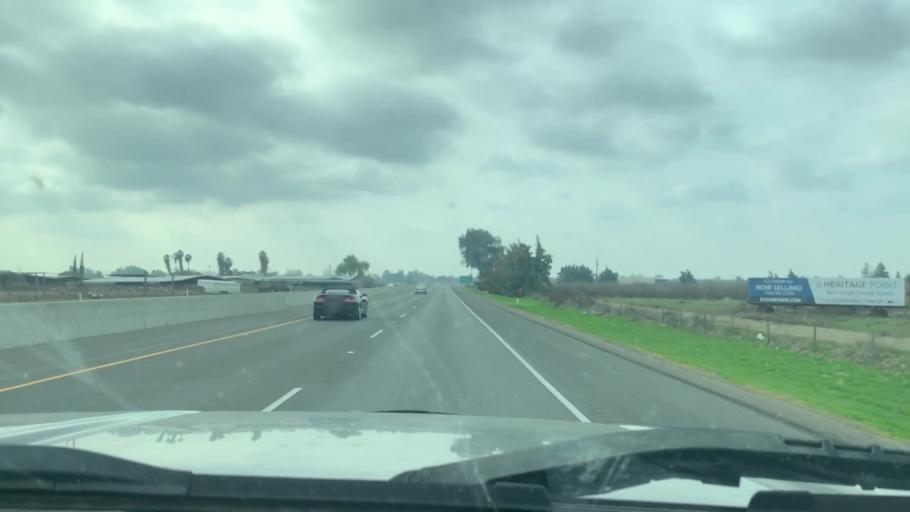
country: US
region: California
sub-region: Kings County
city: Lemoore
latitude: 36.2957
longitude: -119.7595
